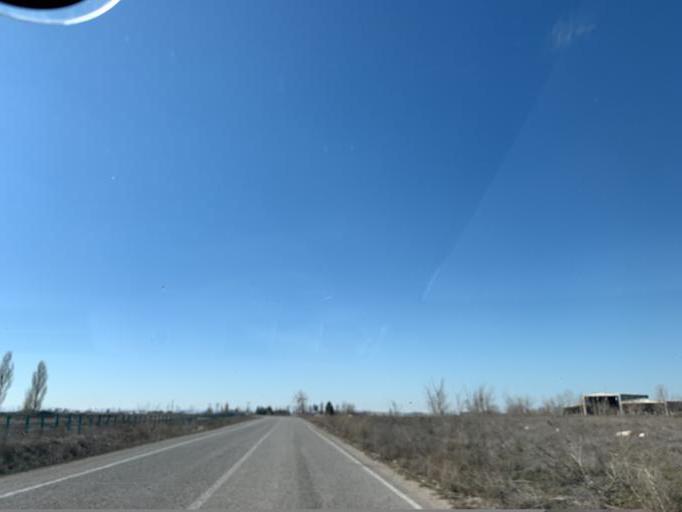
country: TR
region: Konya
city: Cumra
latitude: 37.6145
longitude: 32.7969
